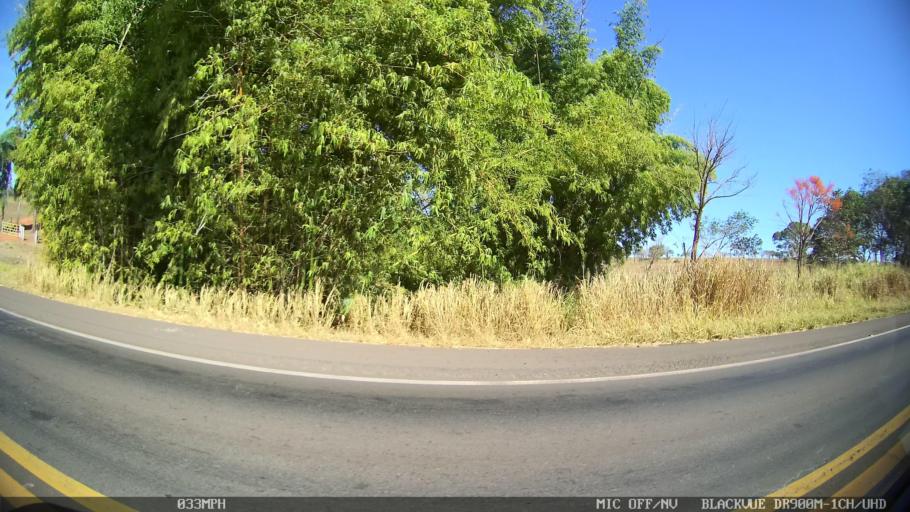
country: BR
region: Sao Paulo
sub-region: Olimpia
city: Olimpia
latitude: -20.6307
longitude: -48.8059
